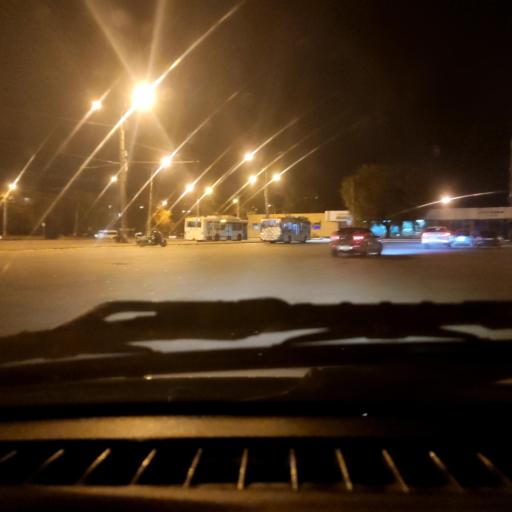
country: RU
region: Samara
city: Zhigulevsk
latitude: 53.4727
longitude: 49.4788
